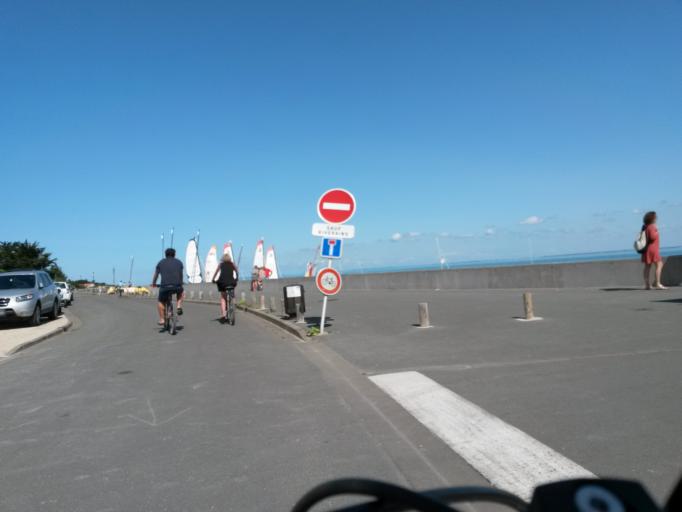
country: FR
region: Poitou-Charentes
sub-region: Departement de la Charente-Maritime
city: La Flotte
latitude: 46.1912
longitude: -1.3298
